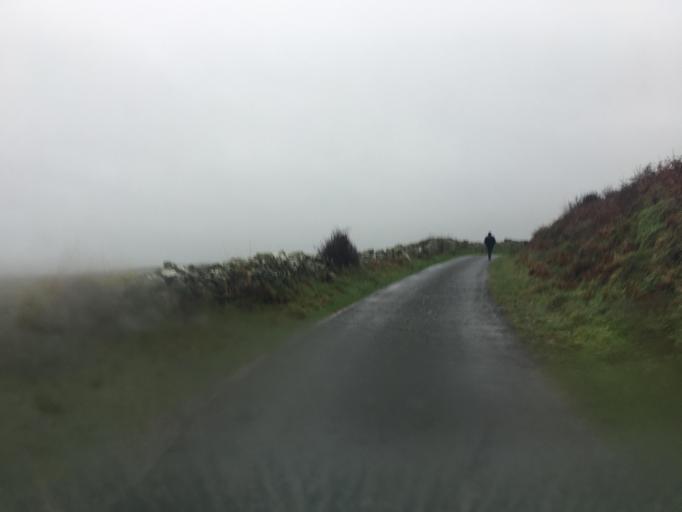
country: FR
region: Lower Normandy
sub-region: Departement de la Manche
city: Beaumont-Hague
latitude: 49.7256
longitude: -1.9236
